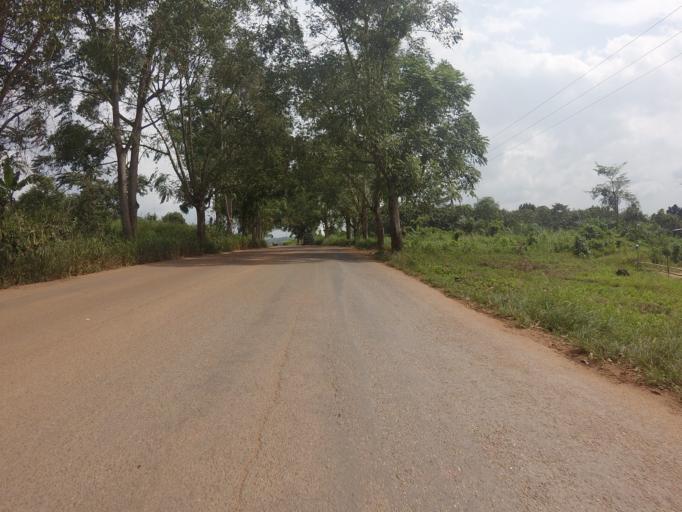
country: GH
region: Eastern
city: Koforidua
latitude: 5.9694
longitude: -0.2226
